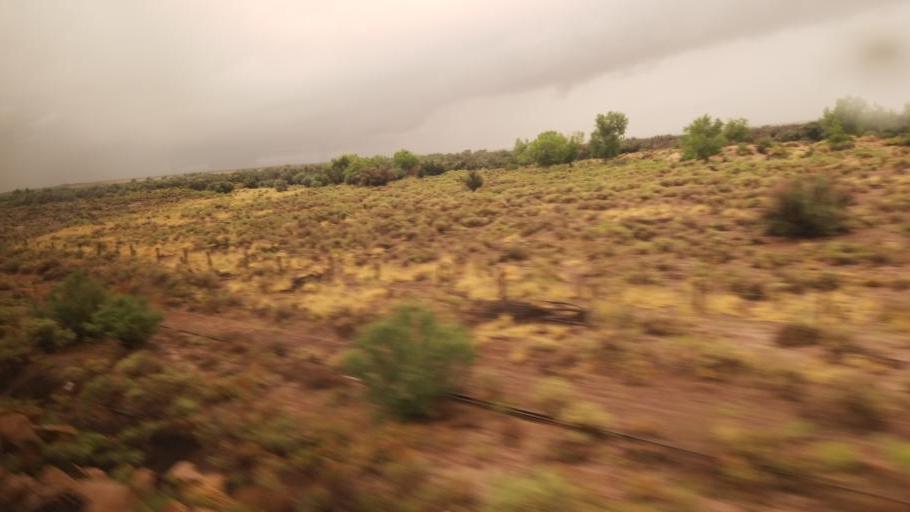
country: US
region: Arizona
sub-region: Navajo County
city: Joseph City
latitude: 34.9672
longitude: -110.4293
